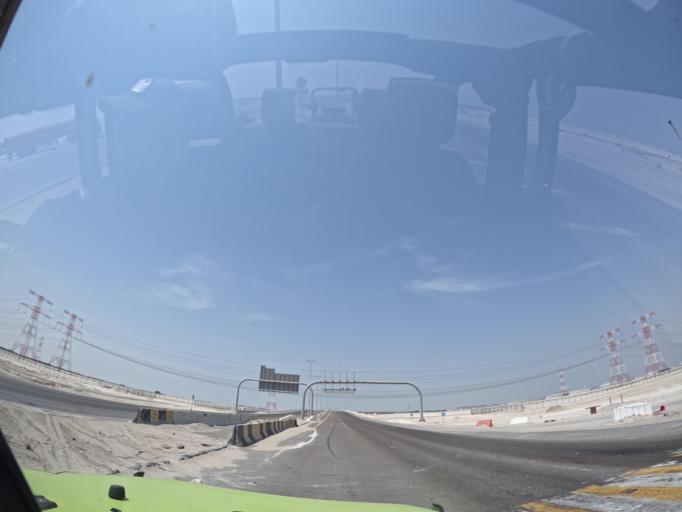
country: AE
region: Abu Dhabi
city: Abu Dhabi
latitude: 24.2528
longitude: 54.4668
